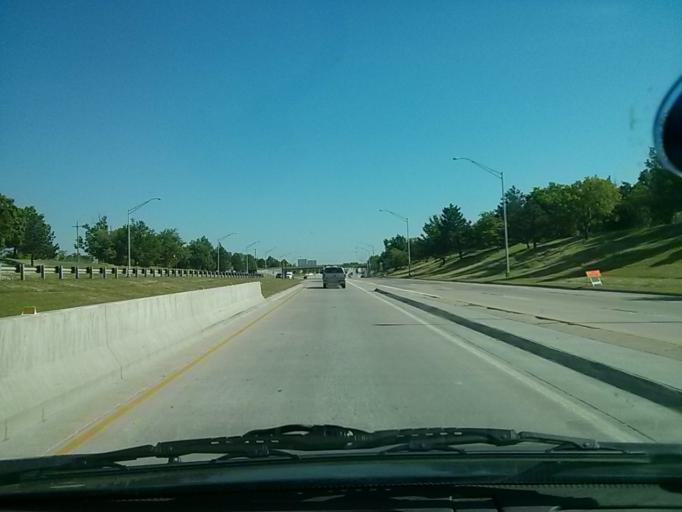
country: US
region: Oklahoma
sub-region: Tulsa County
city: Tulsa
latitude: 36.1629
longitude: -95.9806
